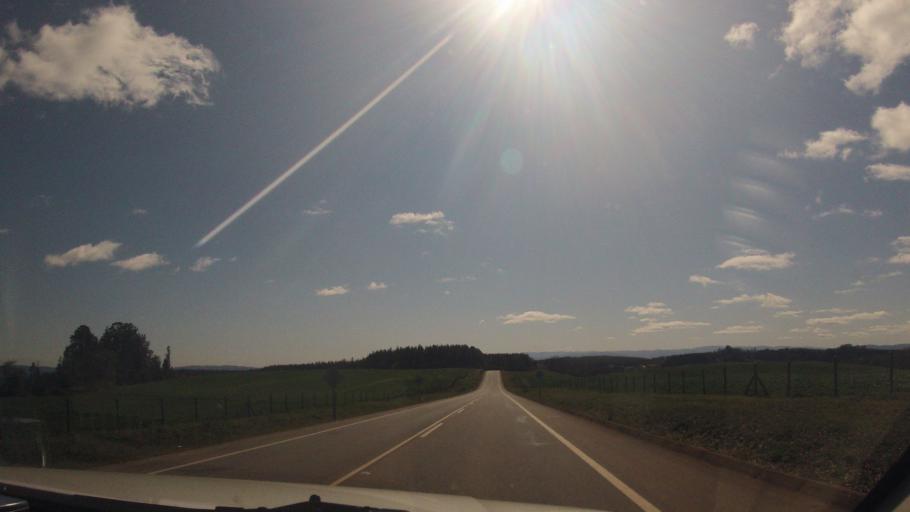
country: CL
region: Araucania
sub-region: Provincia de Malleco
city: Traiguen
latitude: -38.2034
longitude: -72.7984
